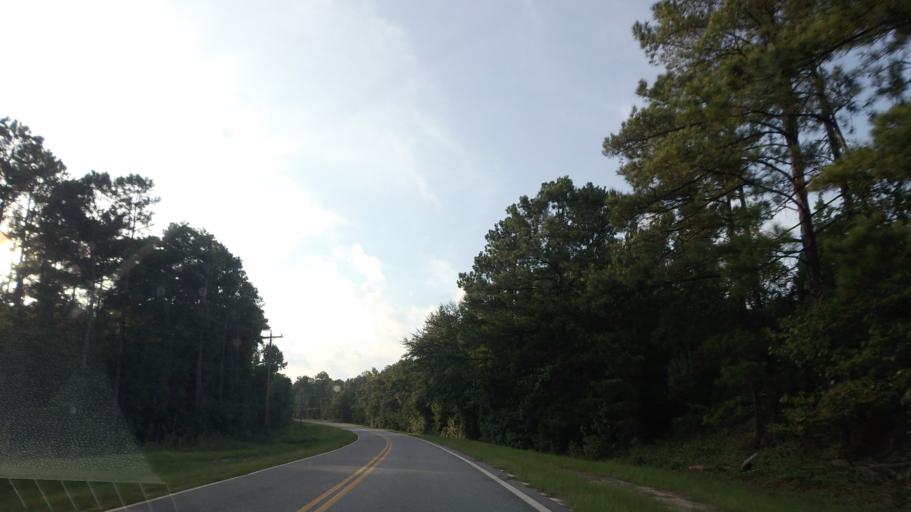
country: US
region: Georgia
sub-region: Wilkinson County
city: Gordon
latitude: 32.8228
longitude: -83.4062
